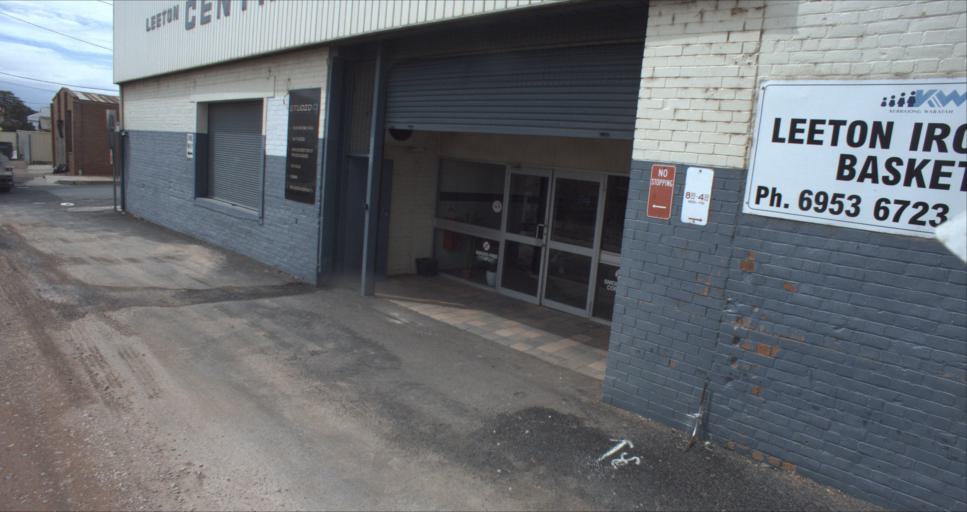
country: AU
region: New South Wales
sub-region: Leeton
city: Leeton
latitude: -34.5509
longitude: 146.4035
